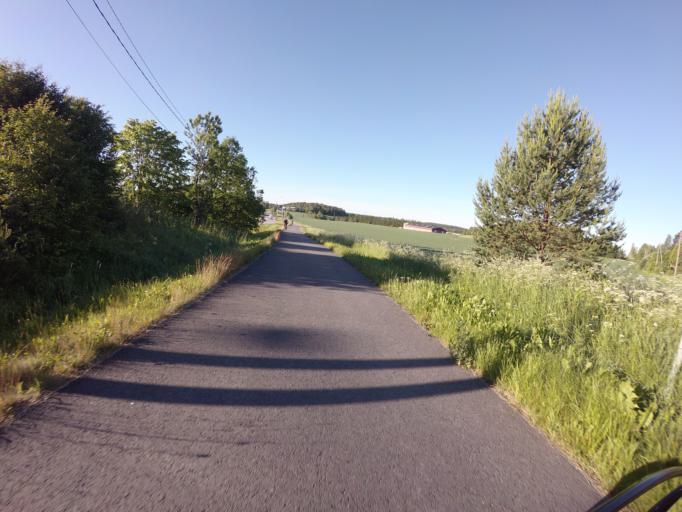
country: FI
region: Varsinais-Suomi
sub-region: Turku
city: Turku
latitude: 60.4998
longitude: 22.3302
